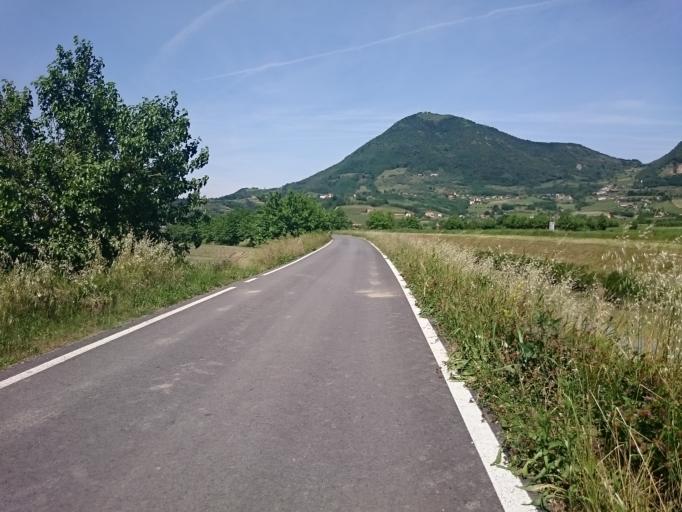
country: IT
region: Veneto
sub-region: Provincia di Padova
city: Vo
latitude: 45.3467
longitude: 11.6288
